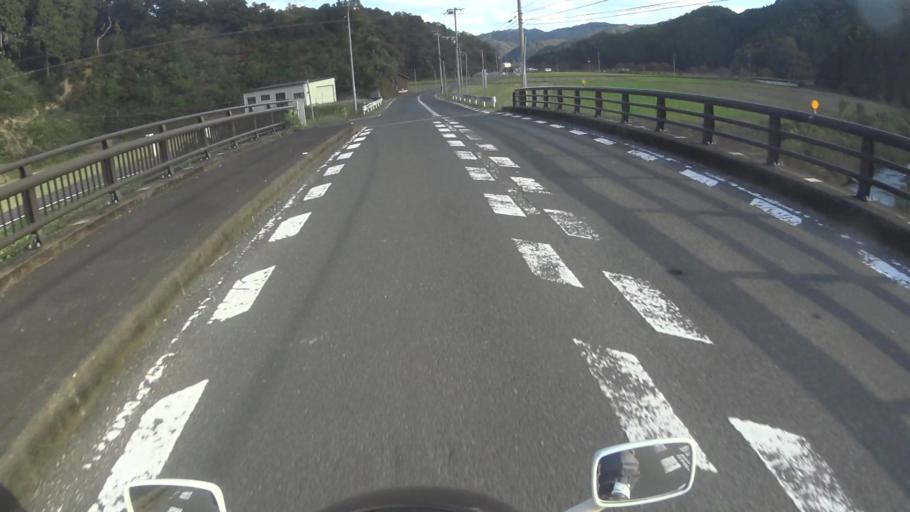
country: JP
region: Kyoto
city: Miyazu
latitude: 35.4376
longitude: 135.2220
